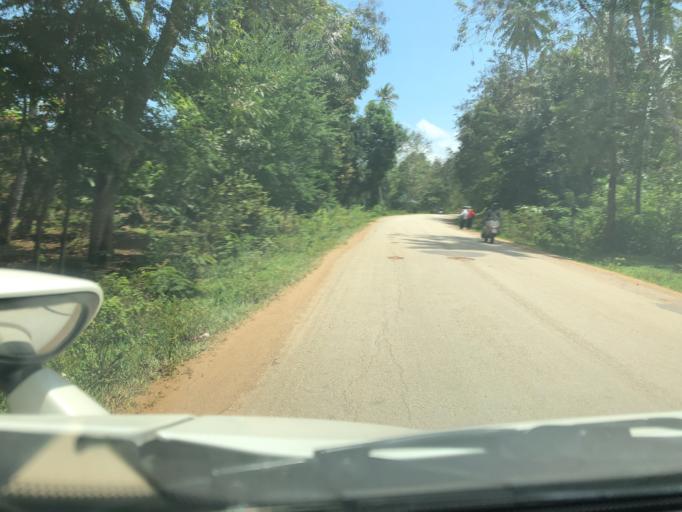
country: TZ
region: Zanzibar Central/South
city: Koani
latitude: -6.0627
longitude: 39.2521
